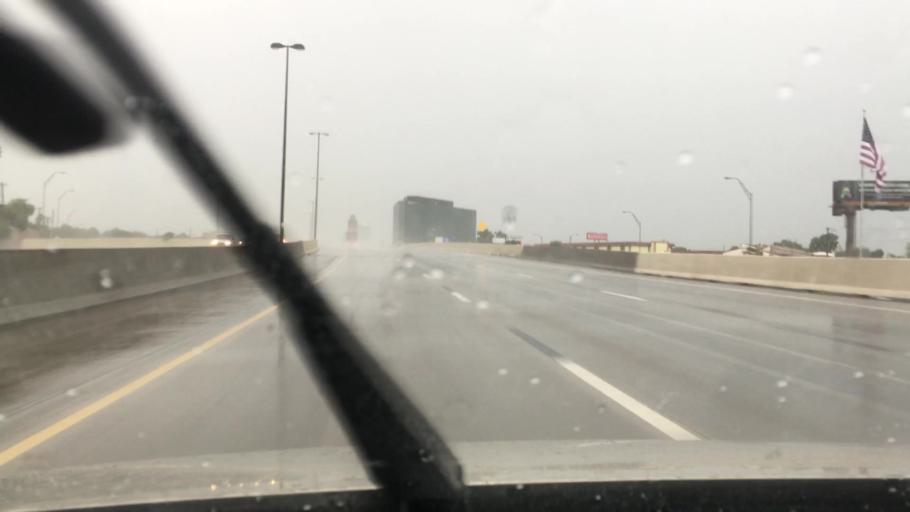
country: US
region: Oklahoma
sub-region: Tulsa County
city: Jenks
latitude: 36.0937
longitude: -95.9246
